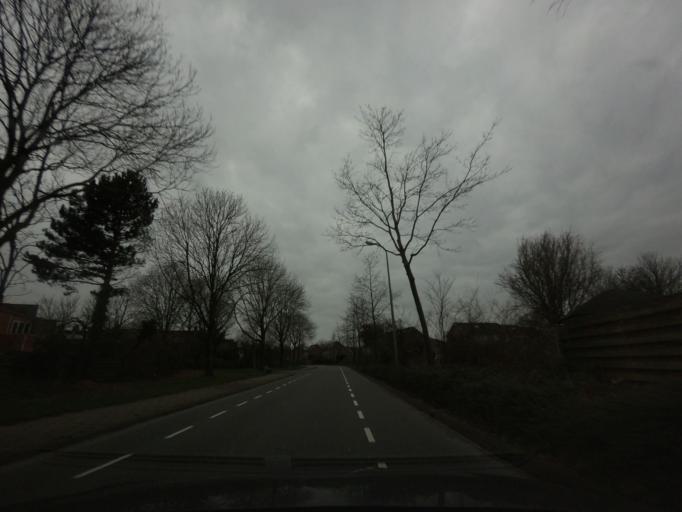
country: NL
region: North Holland
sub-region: Gemeente Schagen
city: Schagen
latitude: 52.7871
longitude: 4.7807
